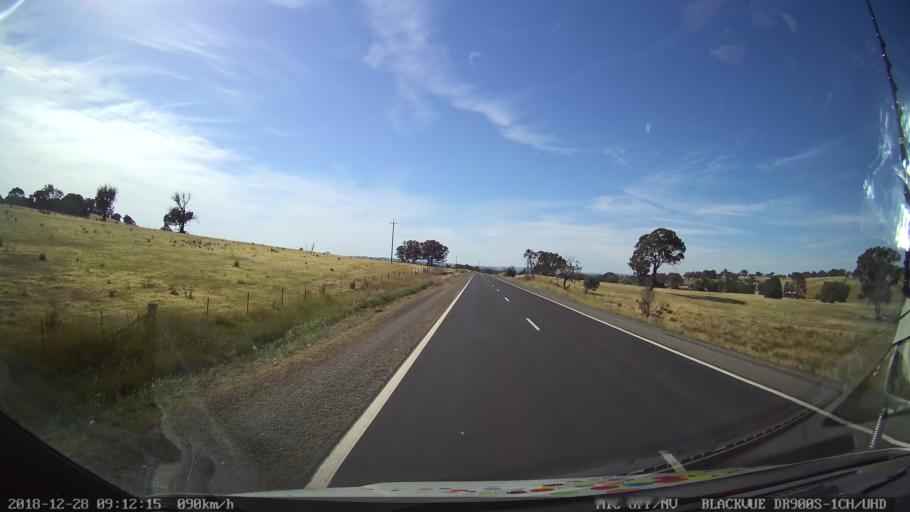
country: AU
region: New South Wales
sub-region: Upper Lachlan Shire
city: Crookwell
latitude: -34.2532
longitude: 149.3403
